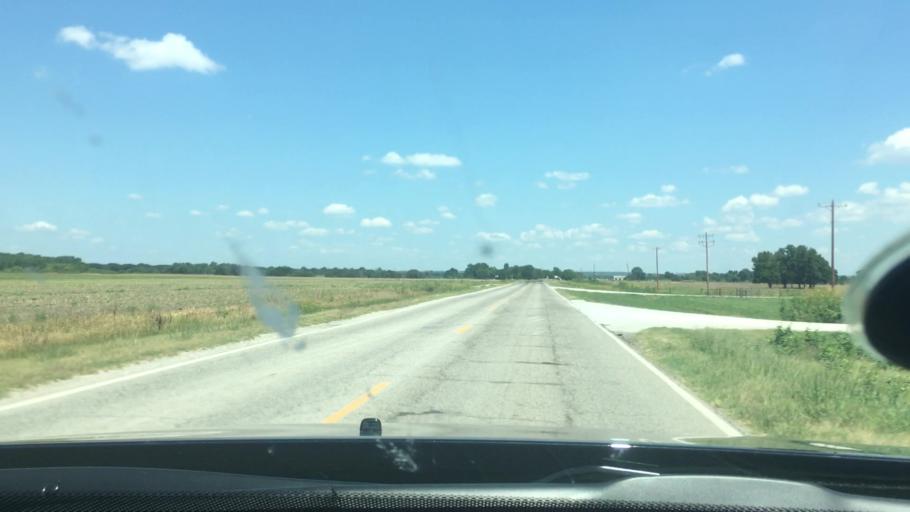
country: US
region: Oklahoma
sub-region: Carter County
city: Dickson
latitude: 34.2214
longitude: -96.9771
